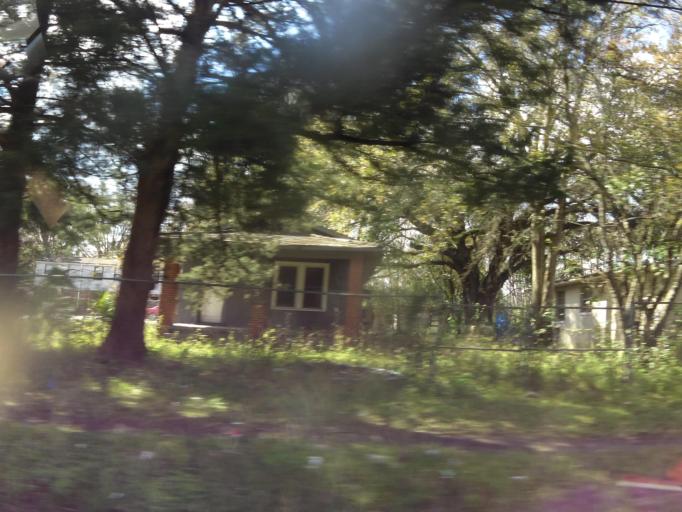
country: US
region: Florida
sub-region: Duval County
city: Jacksonville
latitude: 30.3395
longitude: -81.7141
